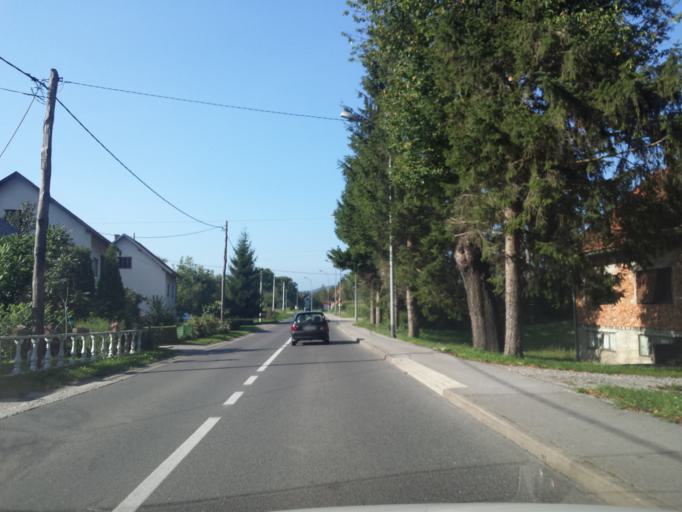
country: HR
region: Karlovacka
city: Ostarije
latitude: 45.2410
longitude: 15.2509
